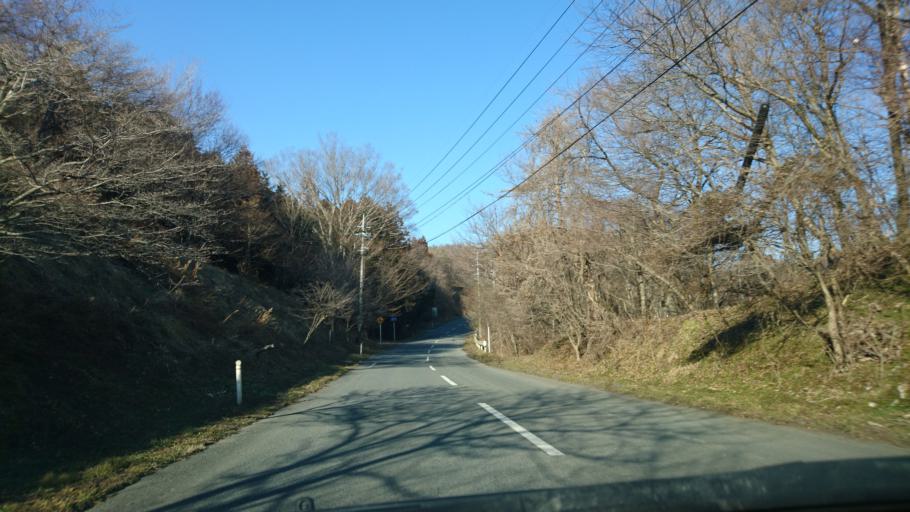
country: JP
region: Iwate
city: Ichinoseki
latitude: 38.8224
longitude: 141.2798
